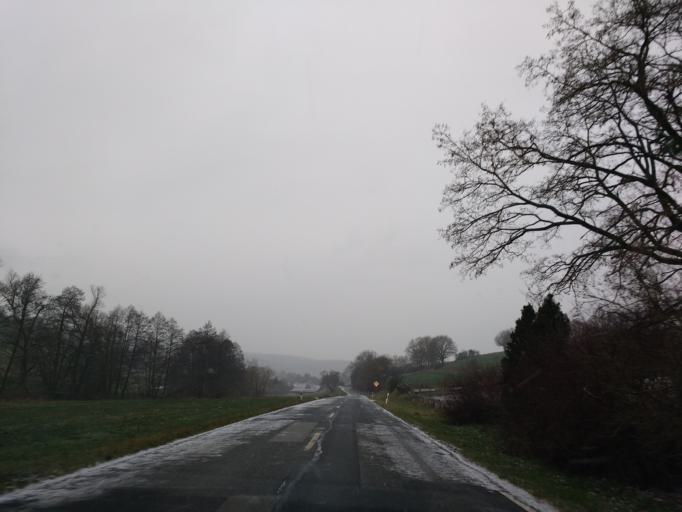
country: DE
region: Hesse
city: Spangenberg
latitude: 51.0924
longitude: 9.7186
